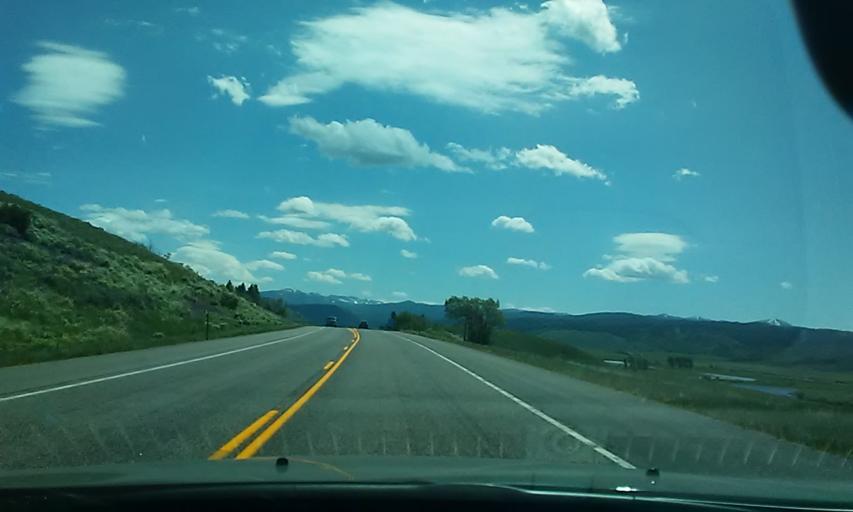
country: US
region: Wyoming
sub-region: Teton County
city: Jackson
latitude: 43.8390
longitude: -110.4486
